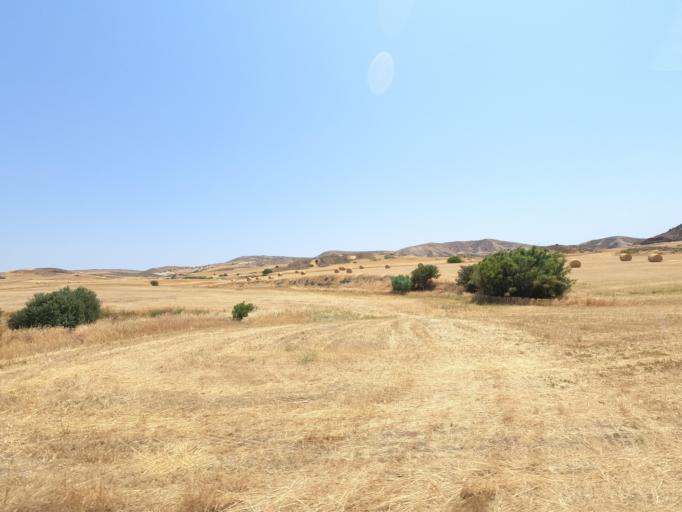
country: CY
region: Larnaka
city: Troulloi
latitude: 35.0216
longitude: 33.6361
